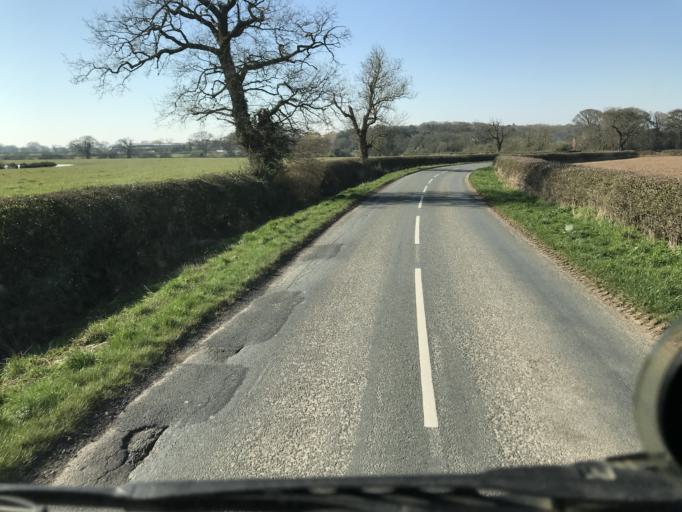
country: GB
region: England
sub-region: Cheshire West and Chester
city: Aldford
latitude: 53.1468
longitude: -2.8389
